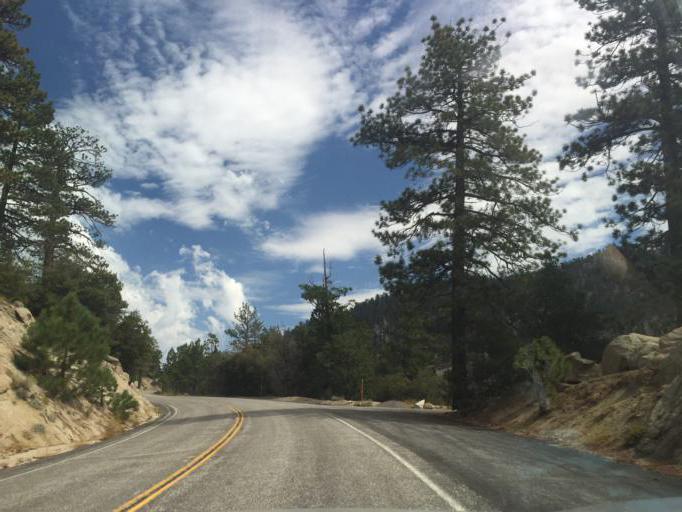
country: US
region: California
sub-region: Los Angeles County
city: Littlerock
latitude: 34.3532
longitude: -117.9448
